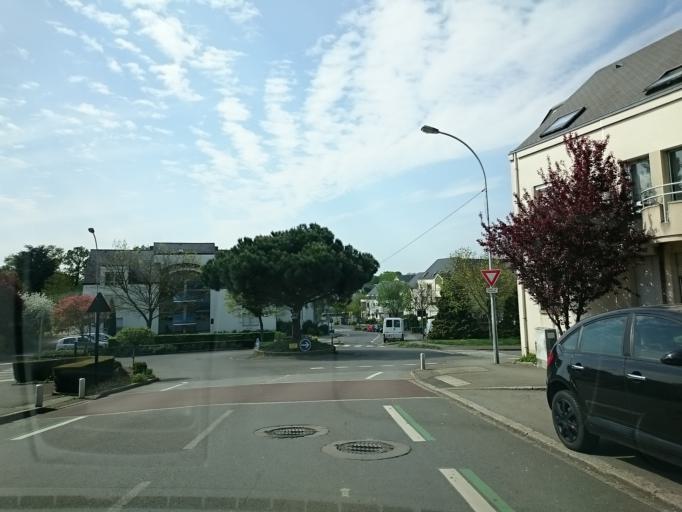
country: FR
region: Brittany
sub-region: Departement d'Ille-et-Vilaine
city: Vern-sur-Seiche
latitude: 48.0441
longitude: -1.6022
